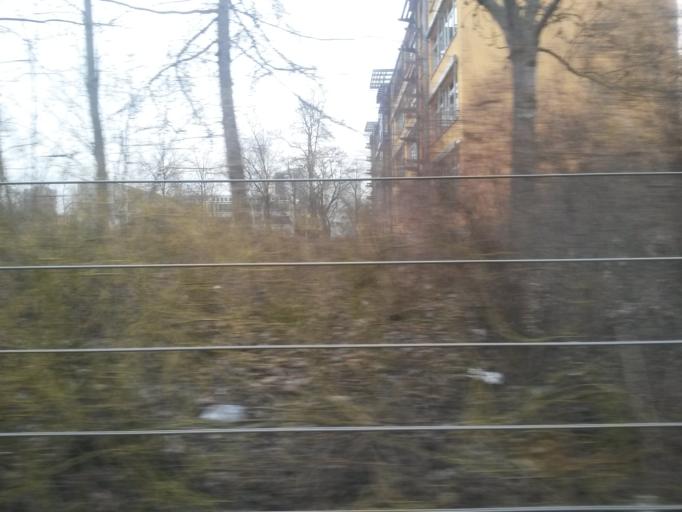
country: DE
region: Thuringia
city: Erfurt
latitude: 51.0046
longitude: 11.0139
